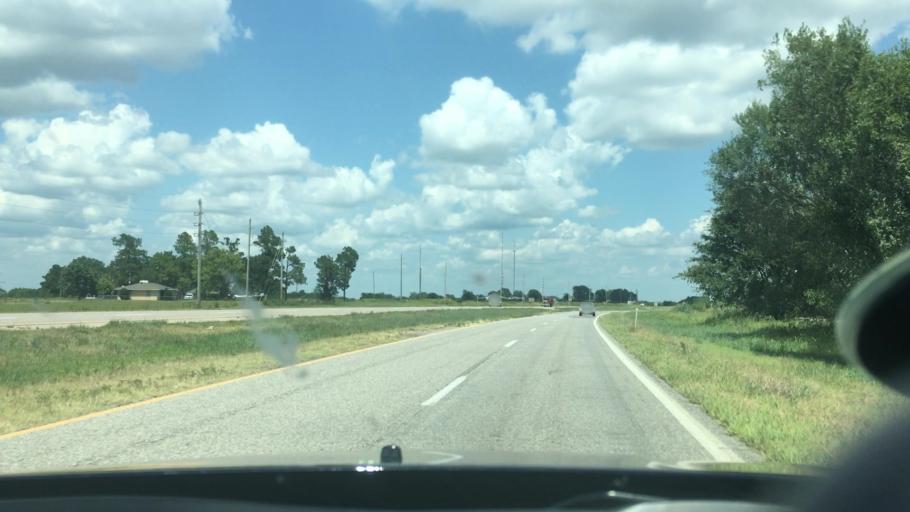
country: US
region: Oklahoma
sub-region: Pontotoc County
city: Ada
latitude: 34.7161
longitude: -96.7240
